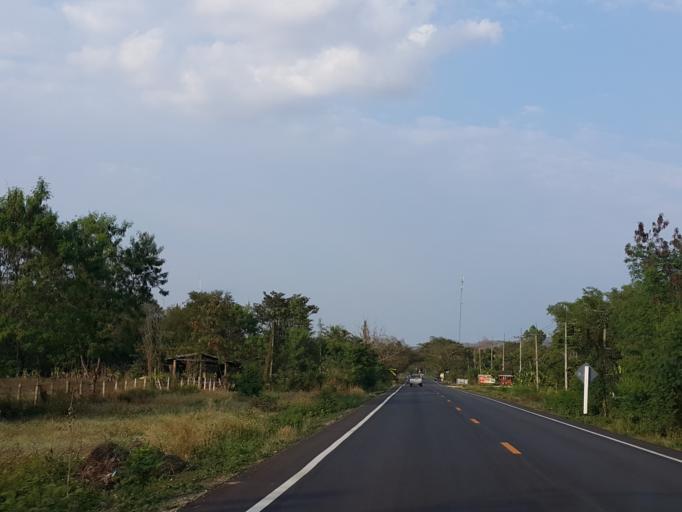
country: TH
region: Lampang
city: Lampang
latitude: 18.4756
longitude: 99.4681
